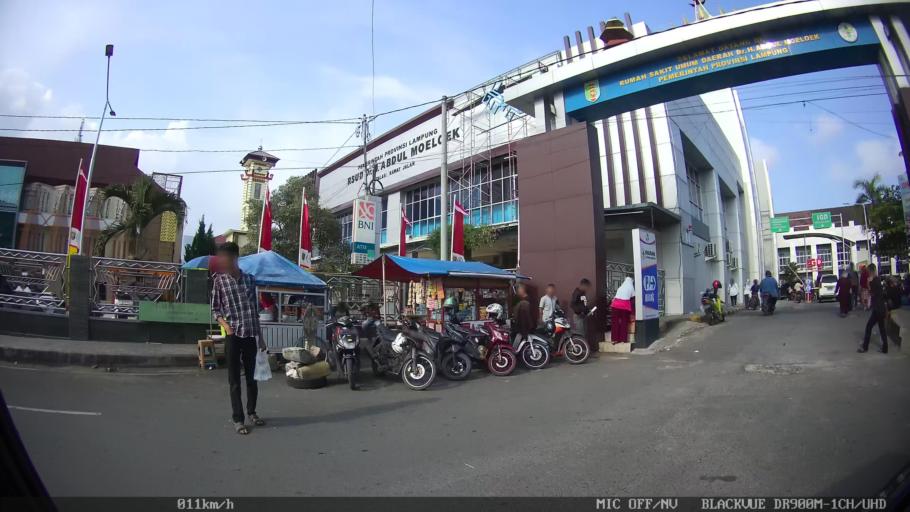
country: ID
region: Lampung
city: Kedaton
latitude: -5.4028
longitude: 105.2586
